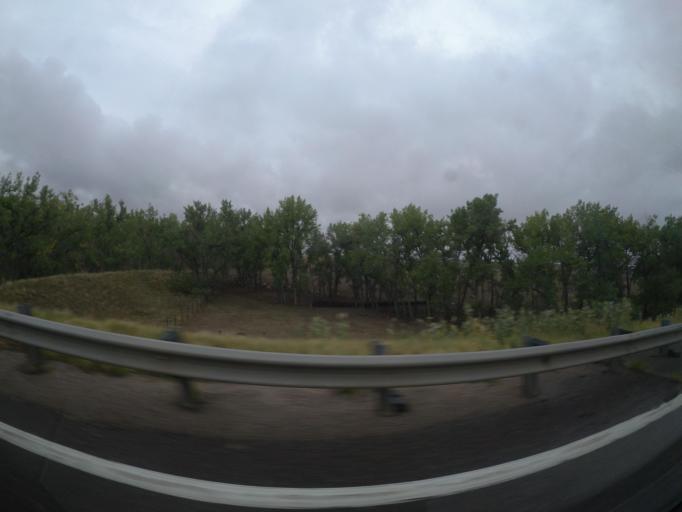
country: US
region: Colorado
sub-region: Arapahoe County
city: Byers
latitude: 39.7398
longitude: -104.1060
